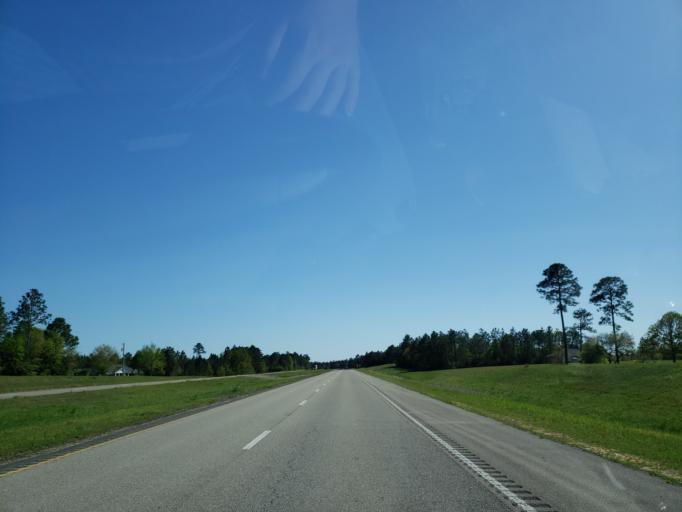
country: US
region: Mississippi
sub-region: Harrison County
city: Lyman
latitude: 30.5284
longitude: -89.0329
